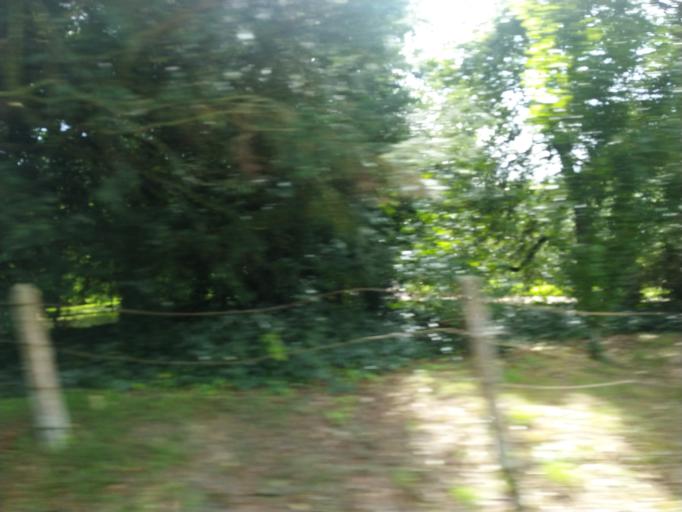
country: GB
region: England
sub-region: Dorset
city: Blandford Forum
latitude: 50.8533
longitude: -2.1469
